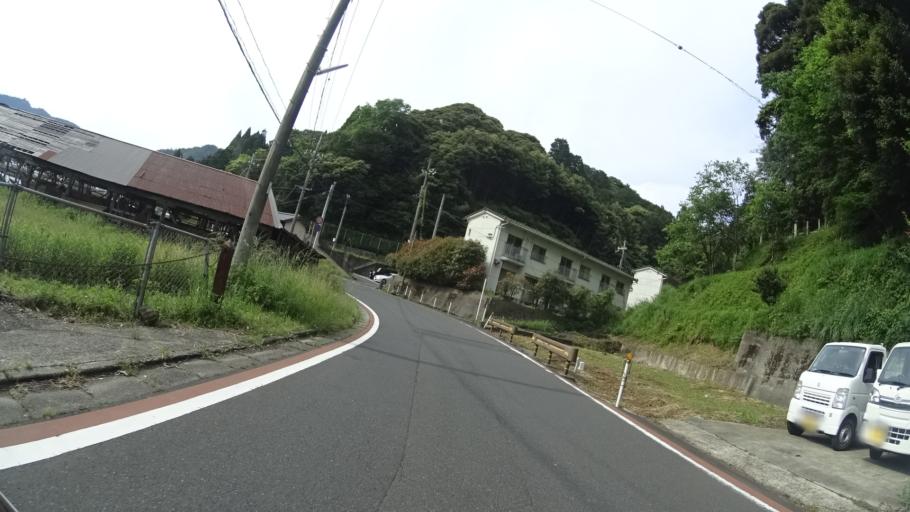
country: JP
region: Kyoto
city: Miyazu
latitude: 35.6708
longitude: 135.2769
